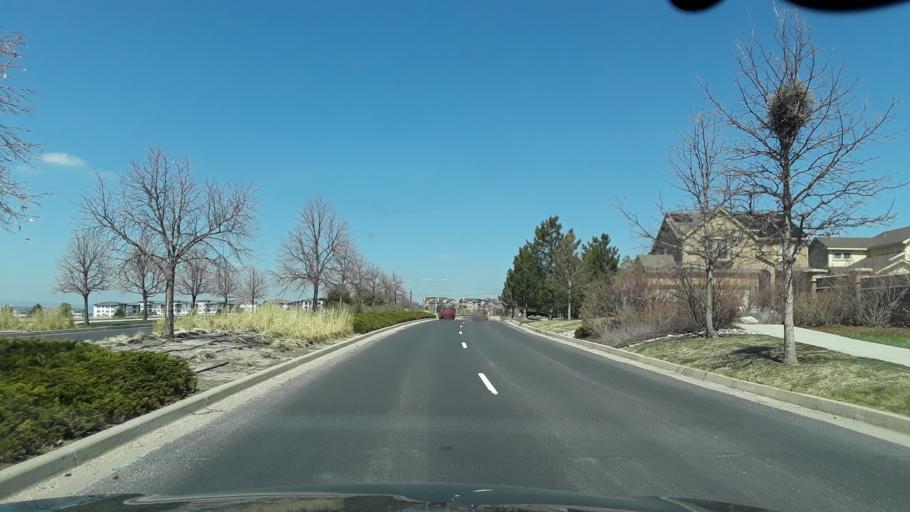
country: US
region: Colorado
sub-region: El Paso County
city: Black Forest
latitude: 38.9690
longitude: -104.7379
